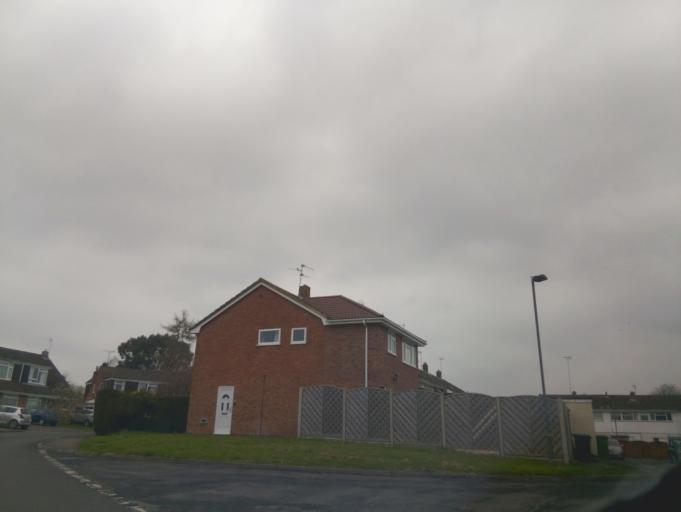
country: GB
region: England
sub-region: South Gloucestershire
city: Charfield
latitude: 51.6252
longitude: -2.4052
